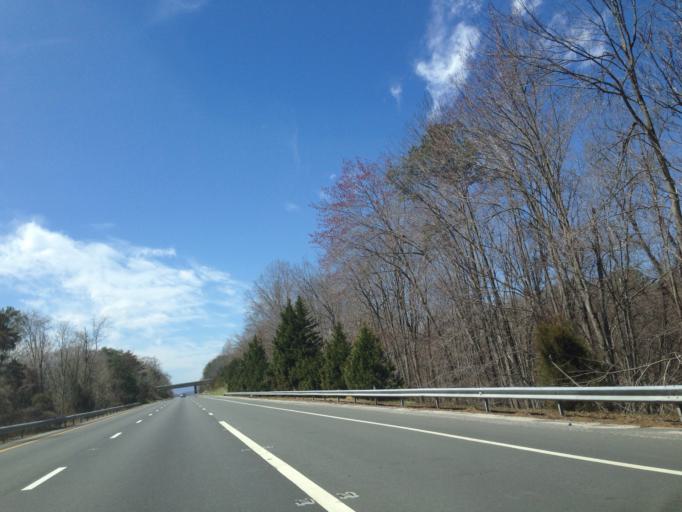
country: US
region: Virginia
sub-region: Albemarle County
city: Crozet
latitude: 38.0338
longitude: -78.6321
